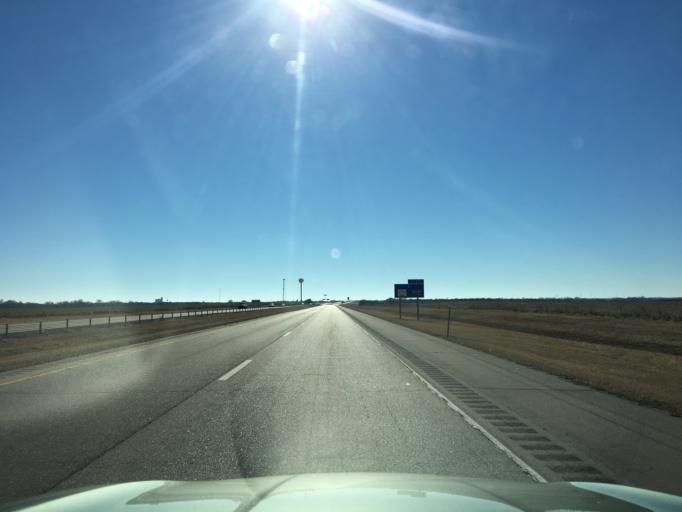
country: US
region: Oklahoma
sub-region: Kay County
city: Blackwell
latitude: 36.9549
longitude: -97.3458
